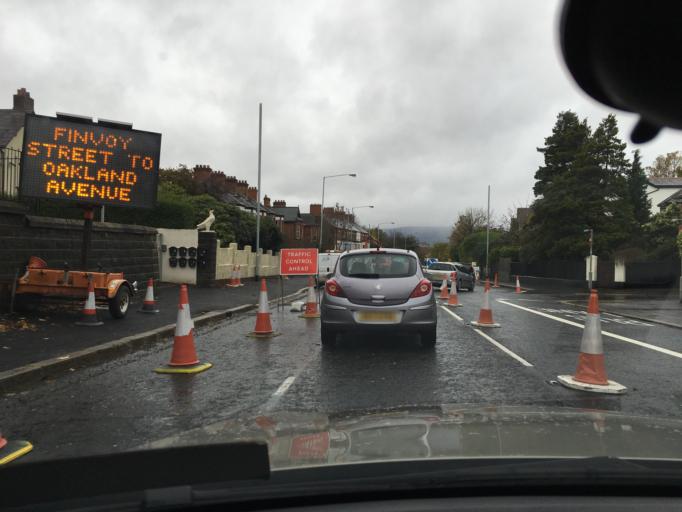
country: GB
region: Northern Ireland
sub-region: Castlereagh District
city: Castlereagh
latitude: 54.5961
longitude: -5.8790
